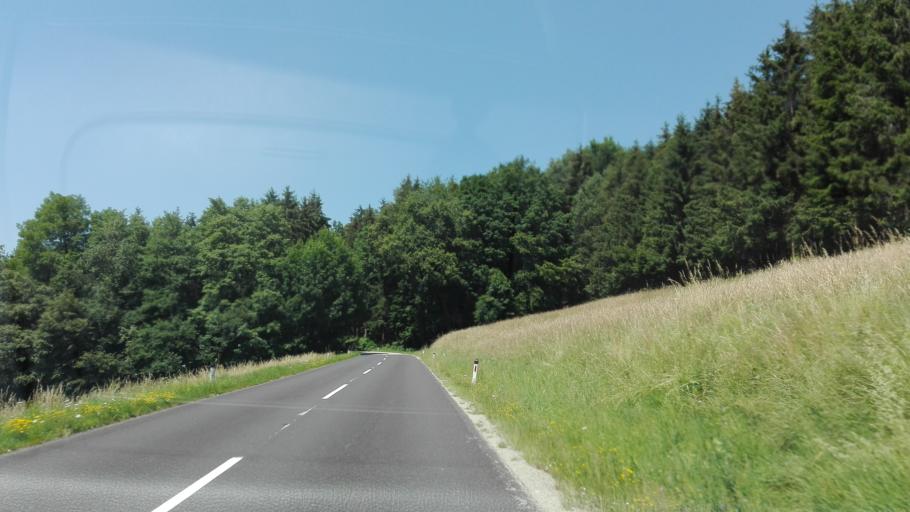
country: AT
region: Upper Austria
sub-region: Politischer Bezirk Grieskirchen
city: Grieskirchen
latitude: 48.3655
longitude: 13.8711
